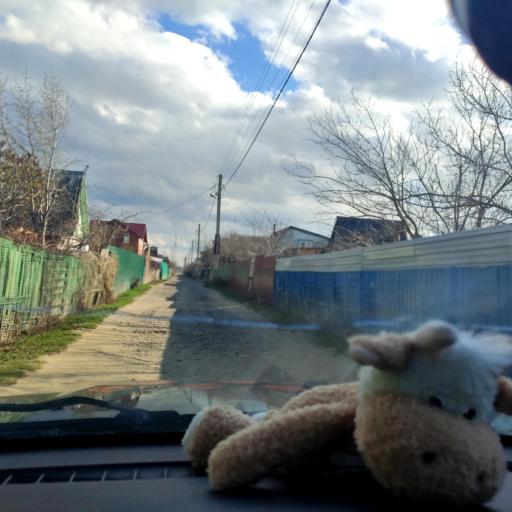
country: RU
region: Samara
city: Tol'yatti
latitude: 53.5932
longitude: 49.3084
